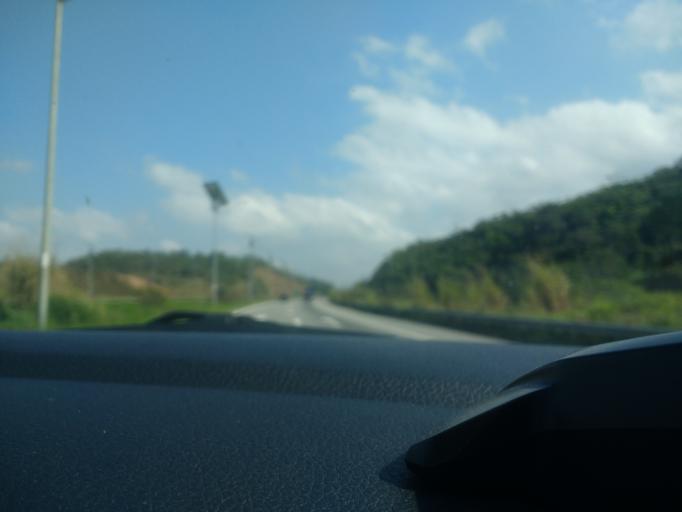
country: BR
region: Rio de Janeiro
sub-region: Queimados
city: Queimados
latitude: -22.6881
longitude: -43.4964
